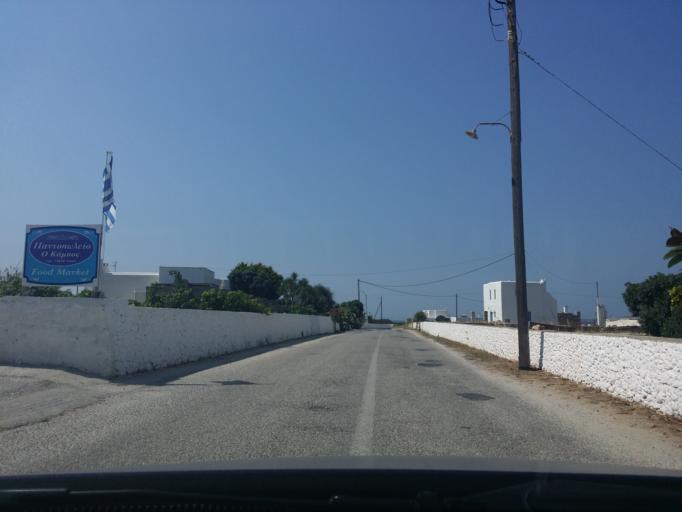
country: GR
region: South Aegean
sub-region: Nomos Kykladon
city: Antiparos
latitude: 37.0242
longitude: 25.1065
